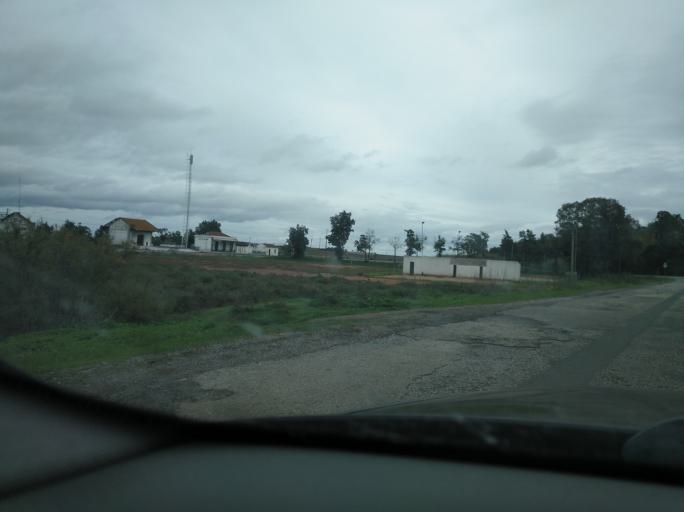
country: PT
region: Faro
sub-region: Vila Real de Santo Antonio
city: Monte Gordo
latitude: 37.1965
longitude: -7.4861
